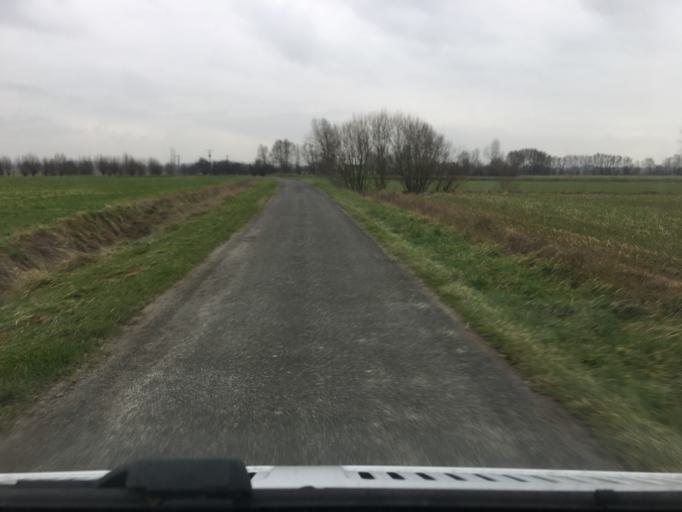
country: FR
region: Picardie
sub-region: Departement de la Somme
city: Pende
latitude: 50.1879
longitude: 1.5481
